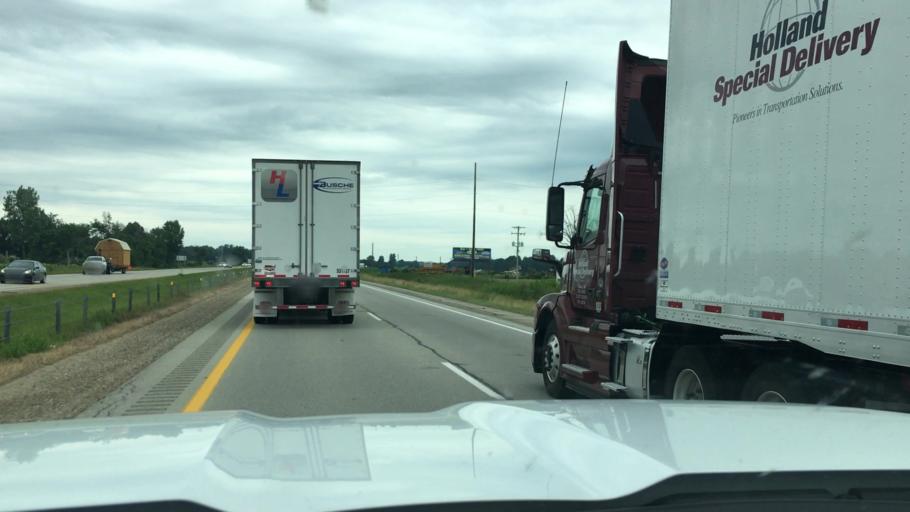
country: US
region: Michigan
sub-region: Allegan County
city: Wayland
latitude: 42.6618
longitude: -85.6621
